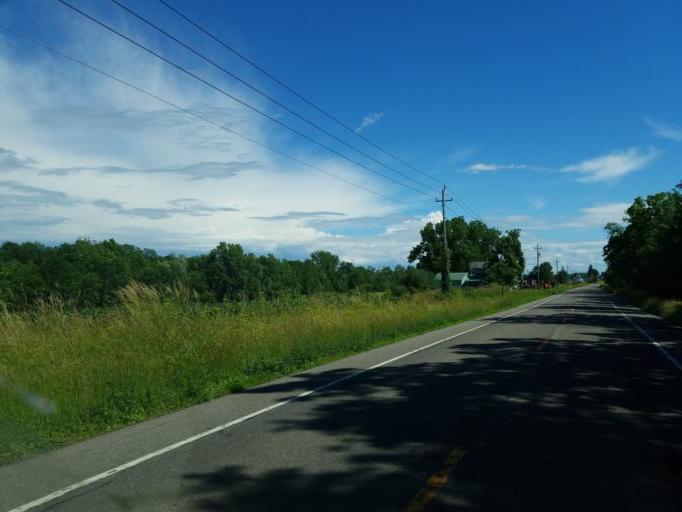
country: US
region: New York
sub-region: Wayne County
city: Clyde
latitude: 43.0005
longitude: -76.8541
